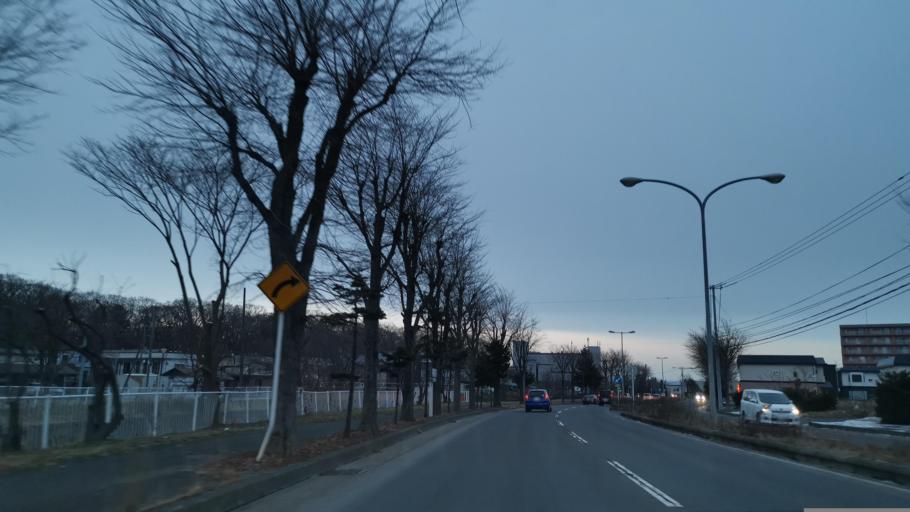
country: JP
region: Hokkaido
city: Chitose
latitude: 42.8139
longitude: 141.6431
